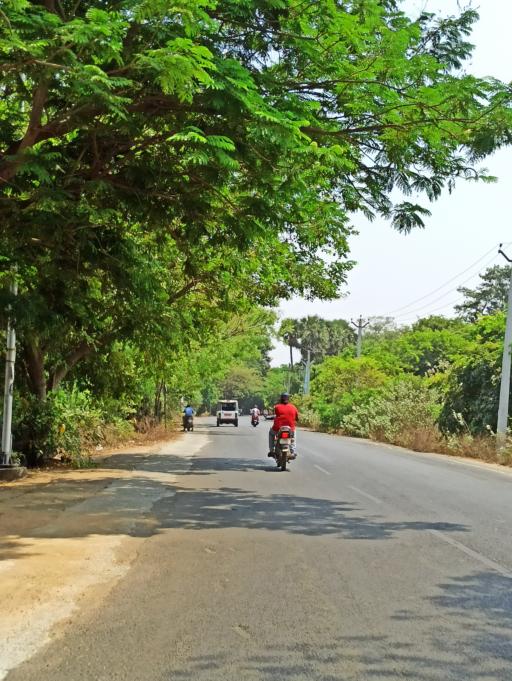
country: IN
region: Tamil Nadu
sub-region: Thiruvallur
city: Chinnasekkadu
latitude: 13.1569
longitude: 80.2440
